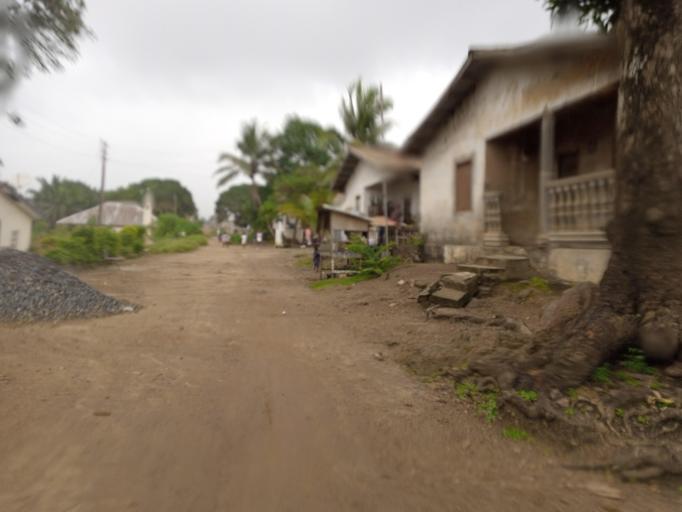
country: SL
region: Eastern Province
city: Kenema
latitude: 7.8800
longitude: -11.1789
